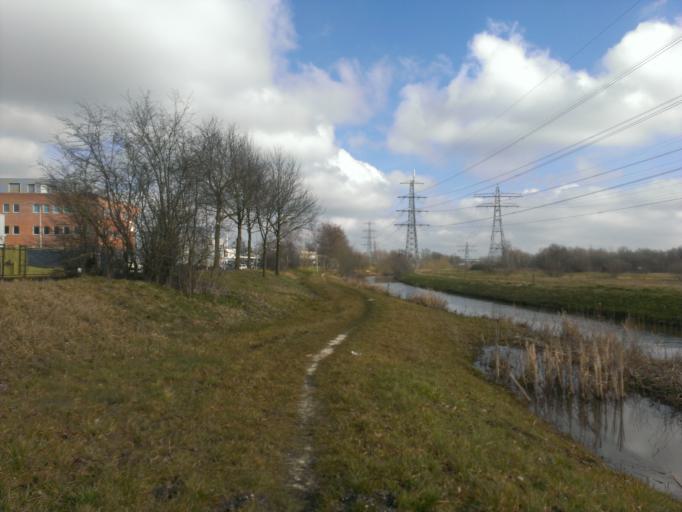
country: NL
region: Drenthe
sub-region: Gemeente Hoogeveen
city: Hoogeveen
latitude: 52.7353
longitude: 6.4682
